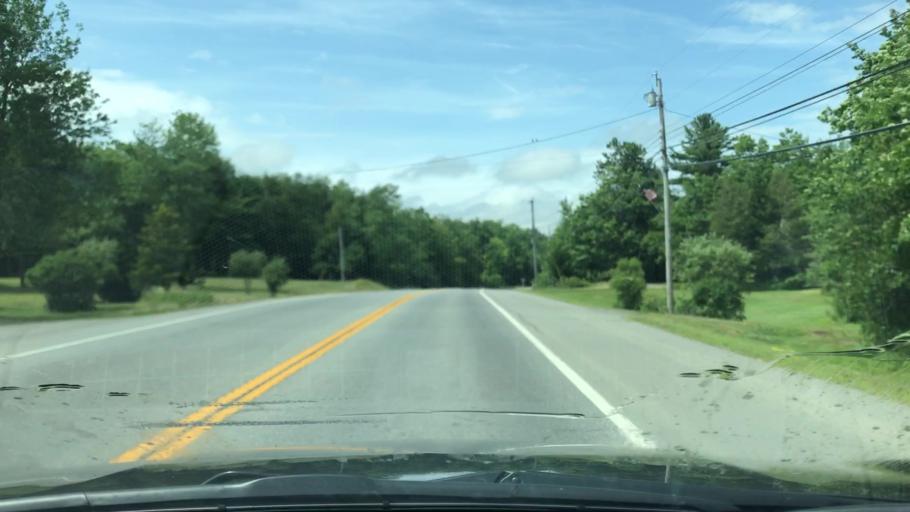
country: US
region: Maine
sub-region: Waldo County
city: Northport
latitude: 44.3589
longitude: -68.9730
